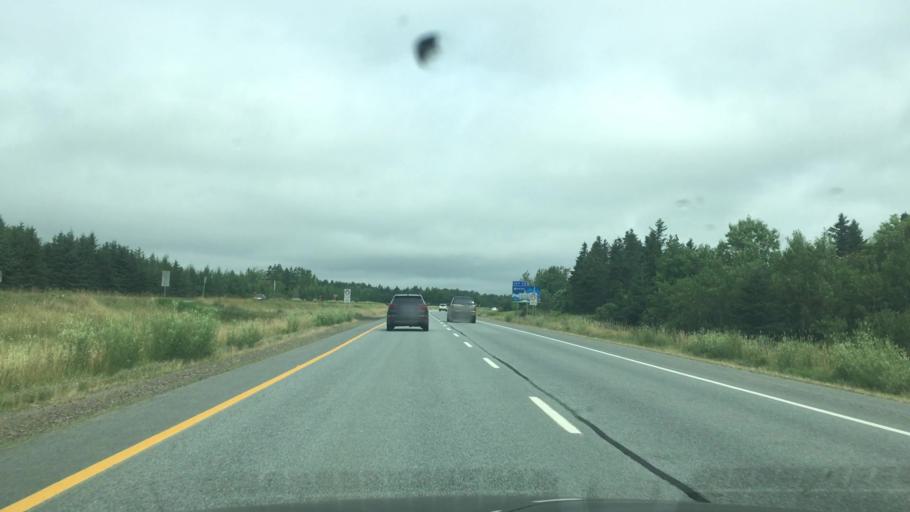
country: CA
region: Nova Scotia
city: Truro
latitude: 45.2991
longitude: -63.3030
